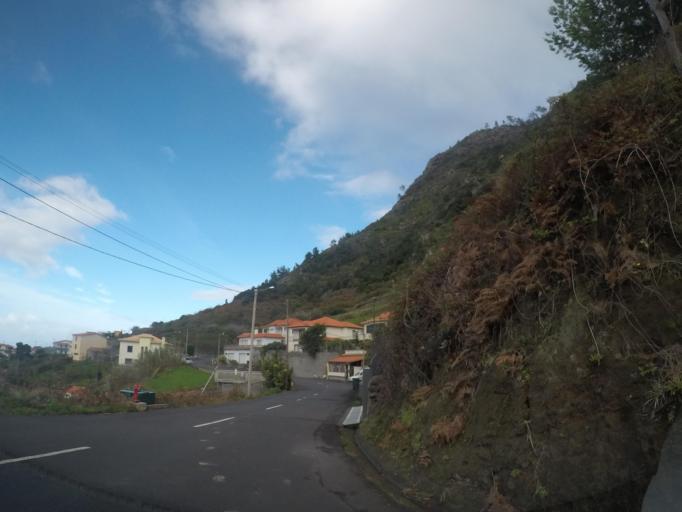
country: PT
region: Madeira
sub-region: Santana
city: Santana
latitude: 32.7846
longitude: -16.8483
